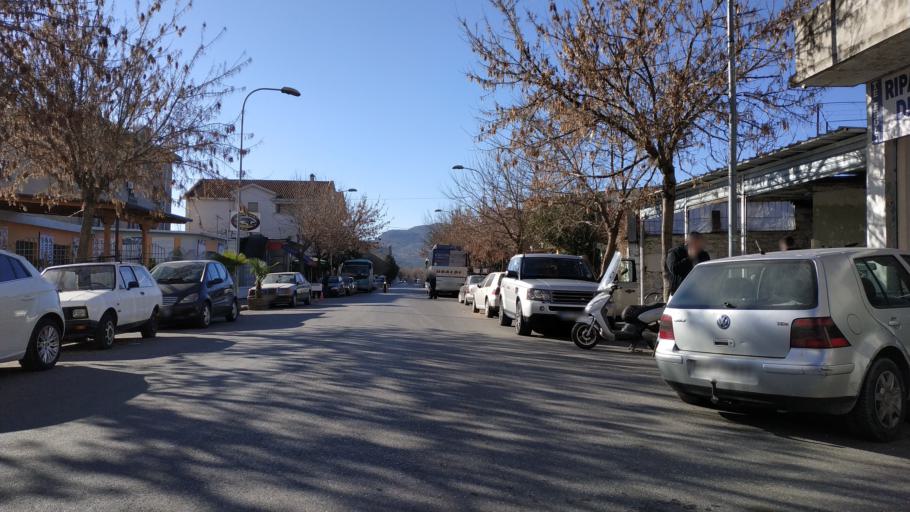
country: AL
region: Shkoder
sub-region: Rrethi i Shkodres
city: Shkoder
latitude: 42.0675
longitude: 19.5058
